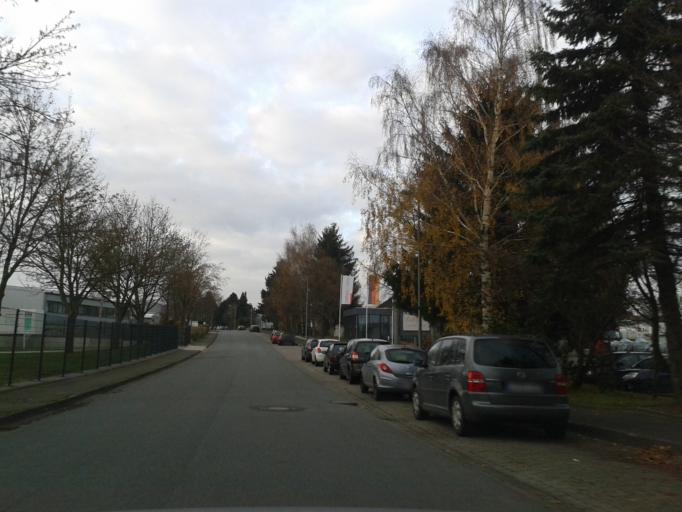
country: DE
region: North Rhine-Westphalia
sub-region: Regierungsbezirk Detmold
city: Blomberg
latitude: 51.9351
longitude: 9.0941
